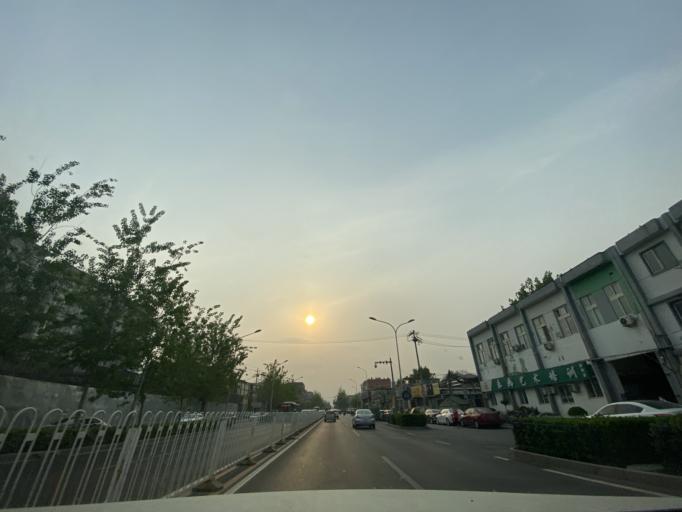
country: CN
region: Beijing
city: Sijiqing
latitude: 39.9277
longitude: 116.2636
